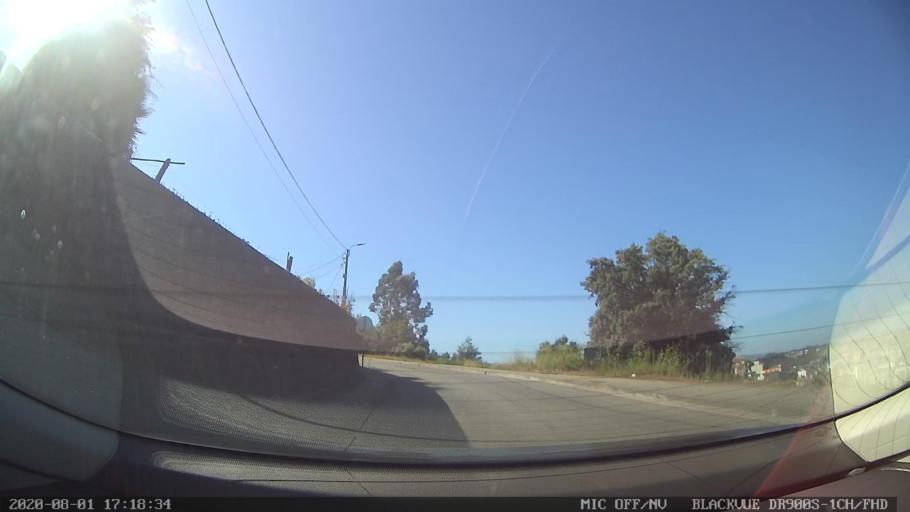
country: PT
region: Porto
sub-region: Santo Tirso
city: Santo Tirso
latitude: 41.3407
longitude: -8.4881
